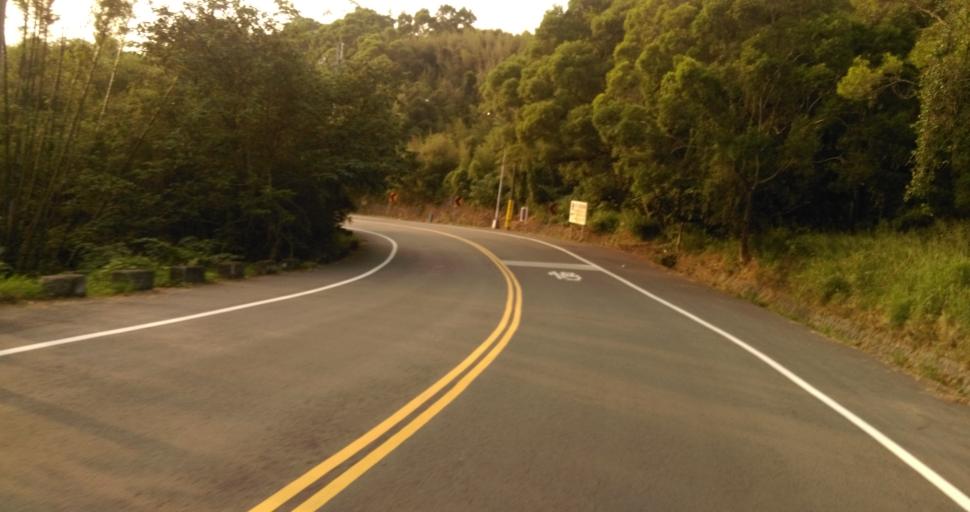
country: TW
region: Taiwan
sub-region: Hsinchu
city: Hsinchu
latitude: 24.7597
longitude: 120.9464
